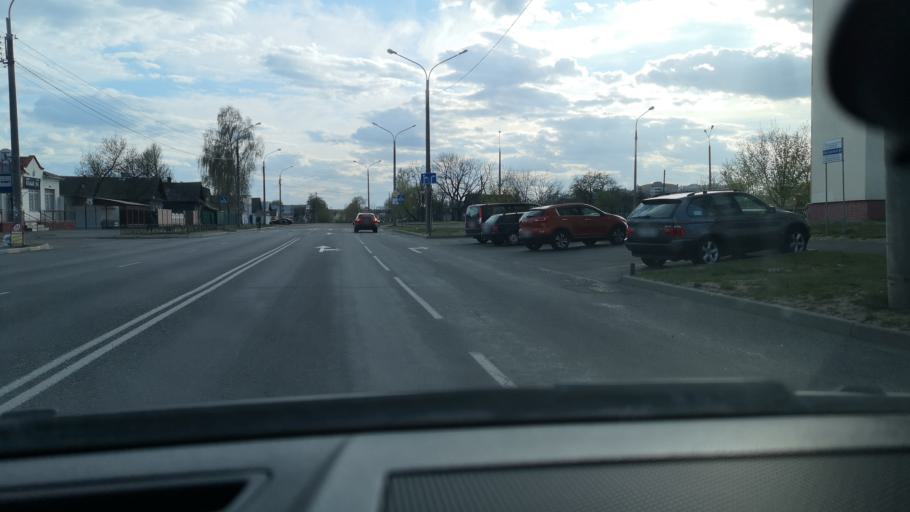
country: BY
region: Gomel
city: Gomel
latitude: 52.3998
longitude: 30.9241
